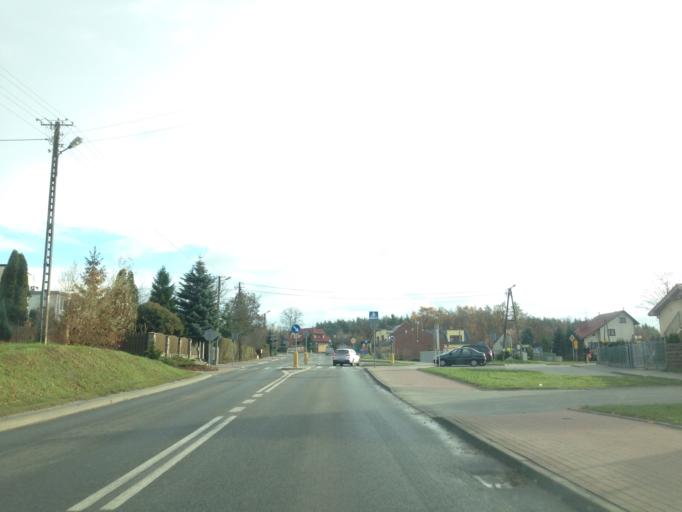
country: PL
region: Pomeranian Voivodeship
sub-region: Powiat gdanski
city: Lublewo Gdanskie
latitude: 54.2840
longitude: 18.5008
